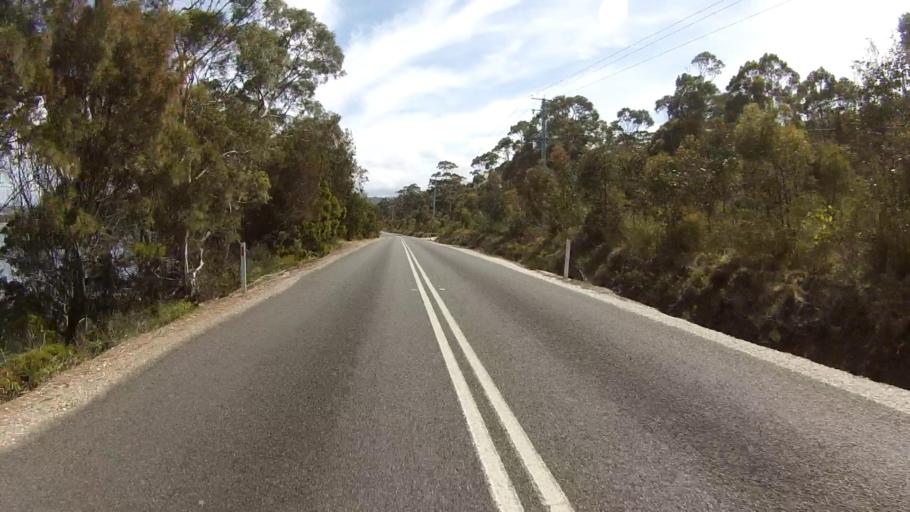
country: AU
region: Tasmania
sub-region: Huon Valley
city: Cygnet
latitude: -43.2614
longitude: 147.1437
